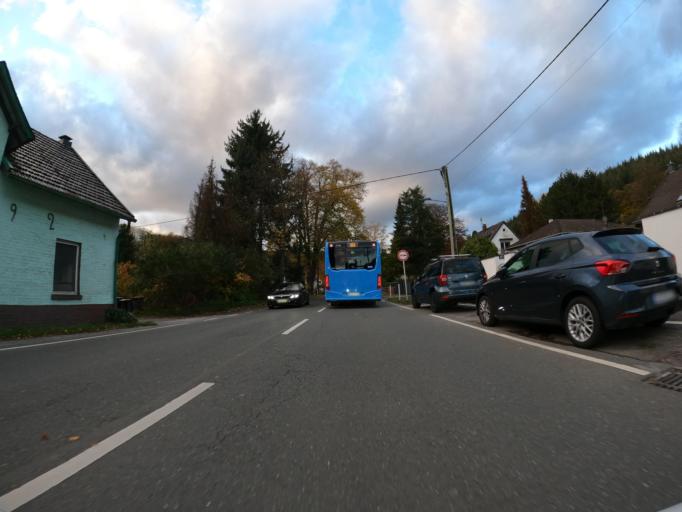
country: DE
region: North Rhine-Westphalia
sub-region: Regierungsbezirk Dusseldorf
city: Solingen
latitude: 51.1941
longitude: 7.1094
